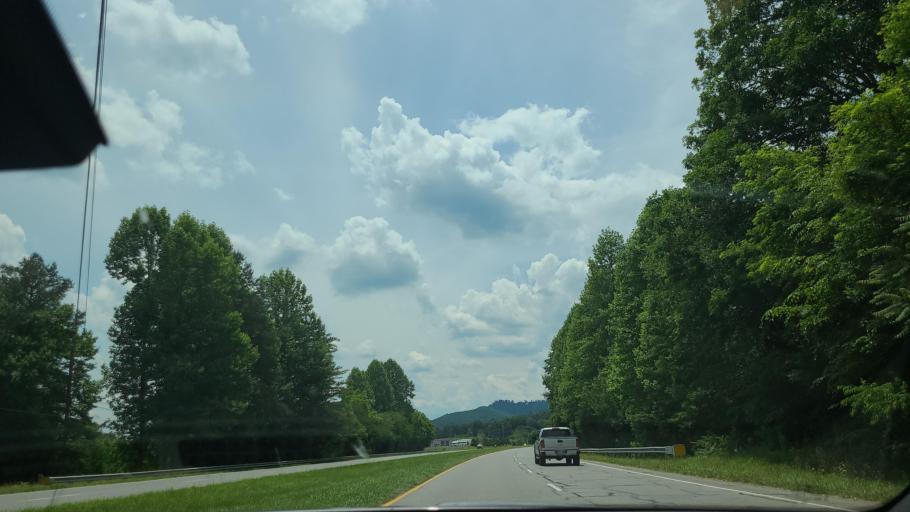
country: US
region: North Carolina
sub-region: Cherokee County
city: Murphy
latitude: 35.0188
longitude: -84.1796
